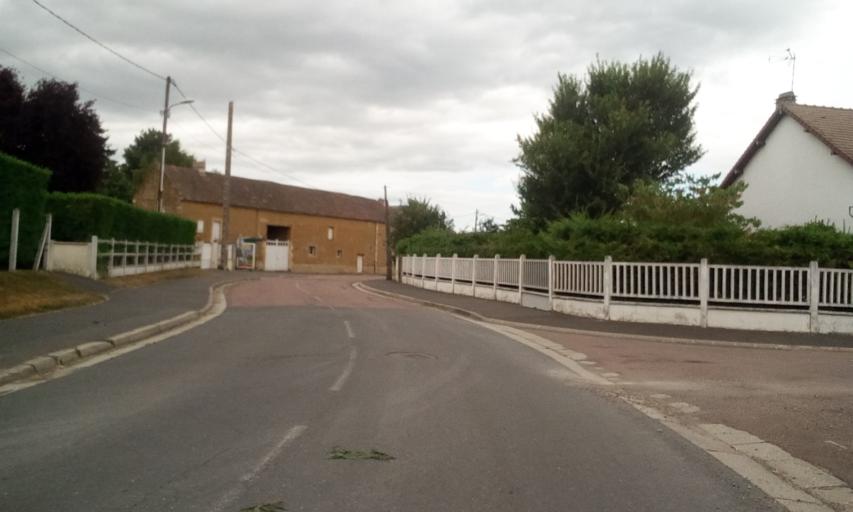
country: FR
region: Lower Normandy
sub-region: Departement du Calvados
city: Sannerville
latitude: 49.1505
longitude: -0.2255
